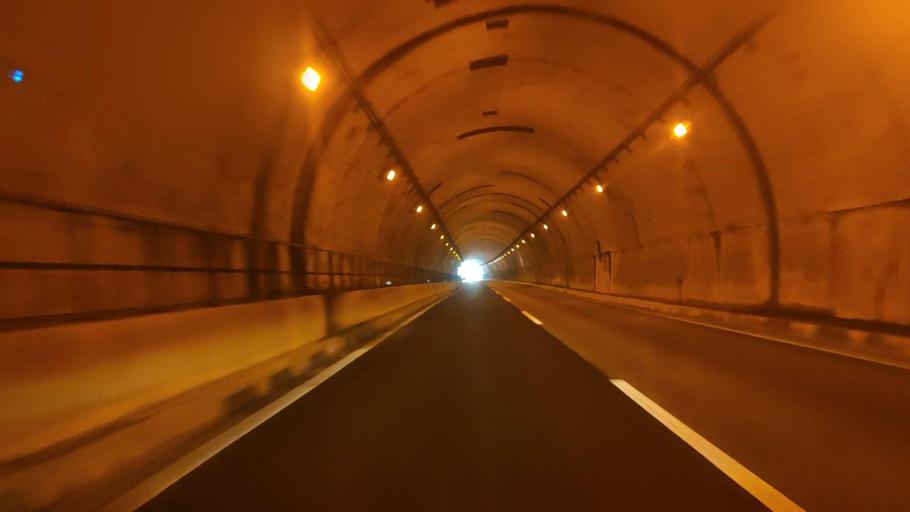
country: JP
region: Miyazaki
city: Miyazaki-shi
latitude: 31.8199
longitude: 131.2600
